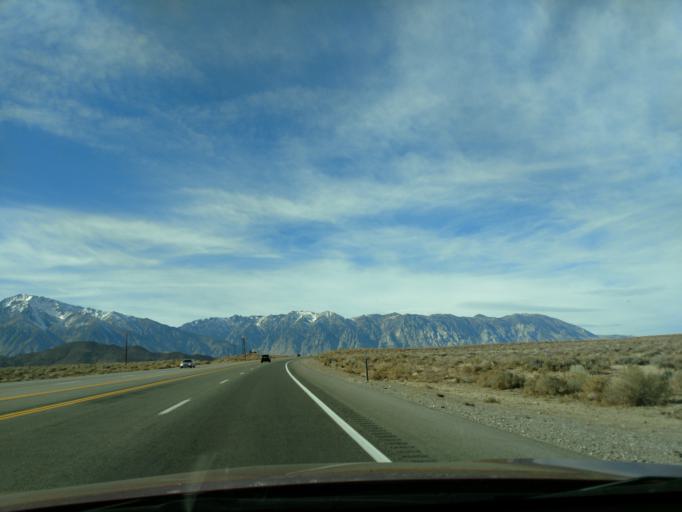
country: US
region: California
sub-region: Inyo County
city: West Bishop
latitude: 37.3762
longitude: -118.4627
